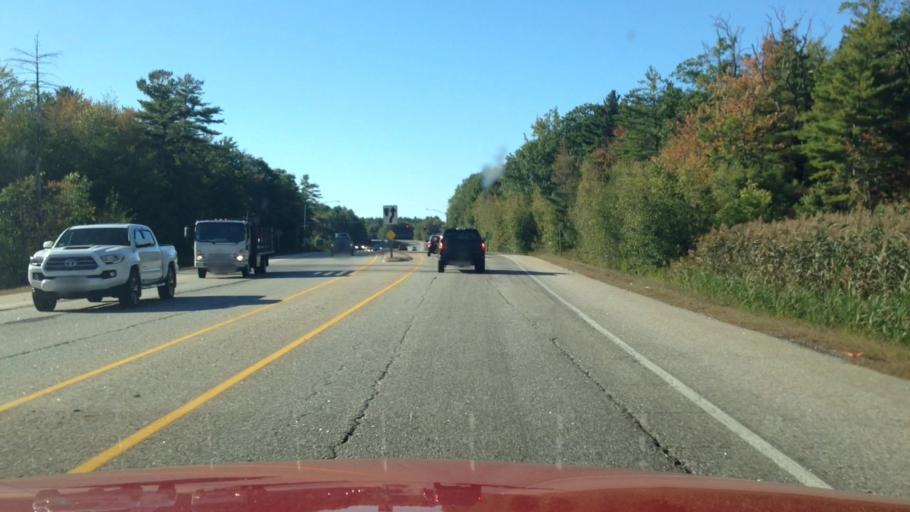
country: US
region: Maine
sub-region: Cumberland County
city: South Portland Gardens
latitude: 43.6694
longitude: -70.3348
